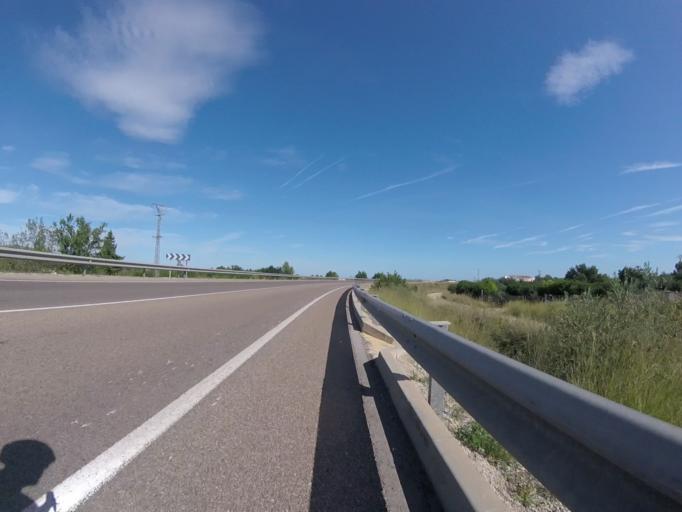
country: ES
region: Valencia
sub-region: Provincia de Castello
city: Peniscola
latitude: 40.3951
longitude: 0.3618
